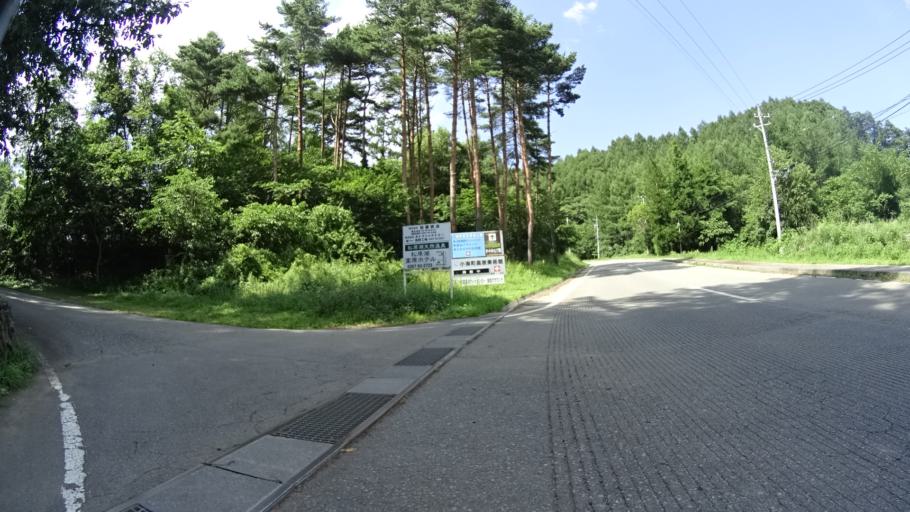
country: JP
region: Nagano
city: Saku
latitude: 36.0538
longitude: 138.4508
